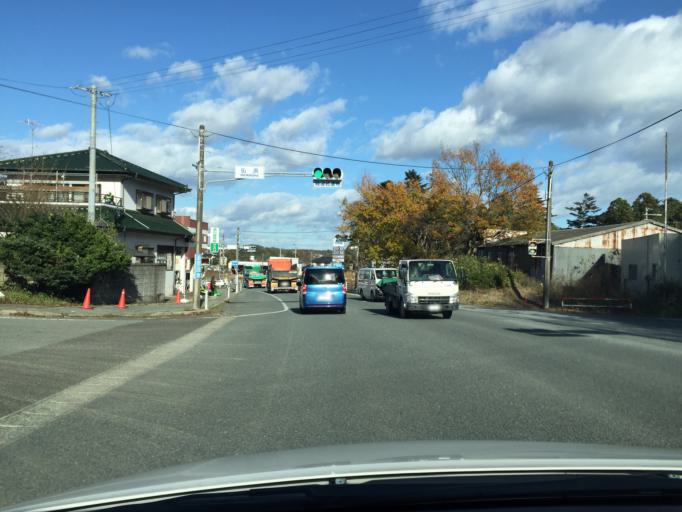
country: JP
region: Fukushima
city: Namie
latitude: 37.3329
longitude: 141.0176
